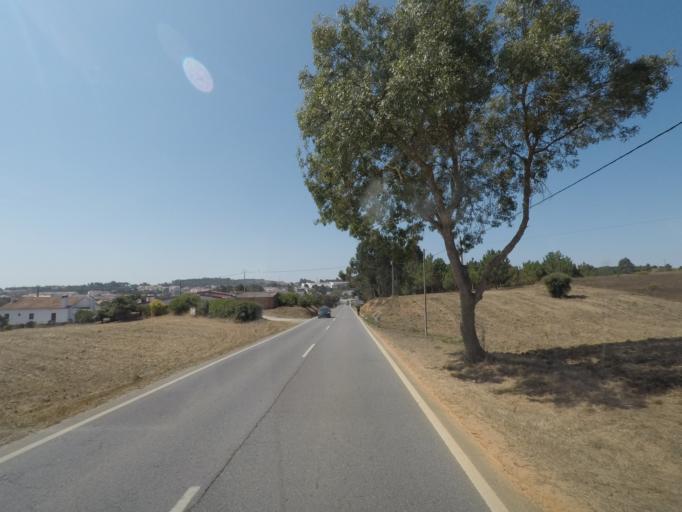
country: PT
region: Beja
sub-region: Odemira
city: Sao Teotonio
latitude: 37.5190
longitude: -8.7057
